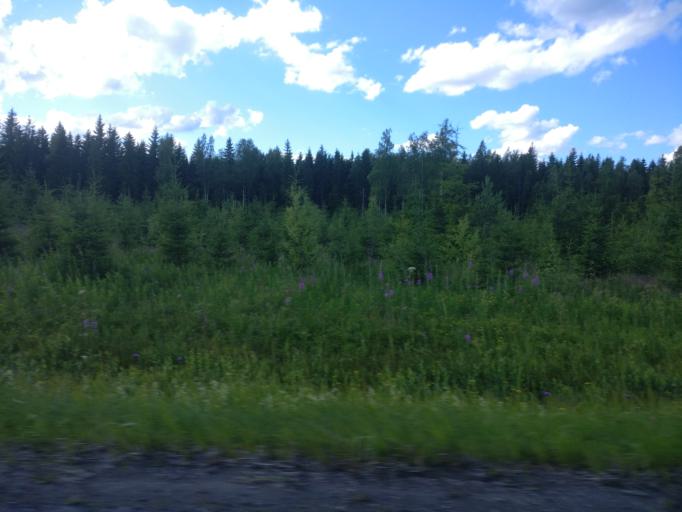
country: FI
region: Uusimaa
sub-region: Helsinki
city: Hyvinge
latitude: 60.5910
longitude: 24.8476
